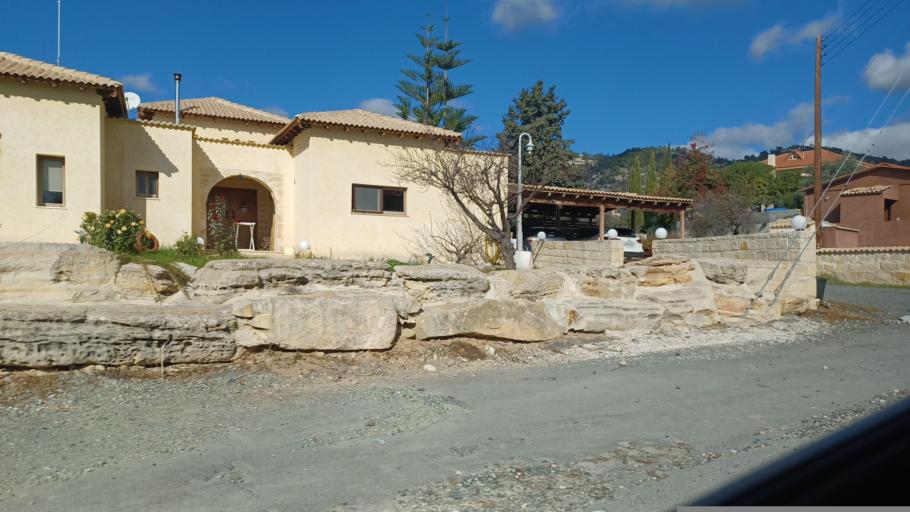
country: CY
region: Limassol
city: Pano Polemidia
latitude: 34.7872
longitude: 32.9765
